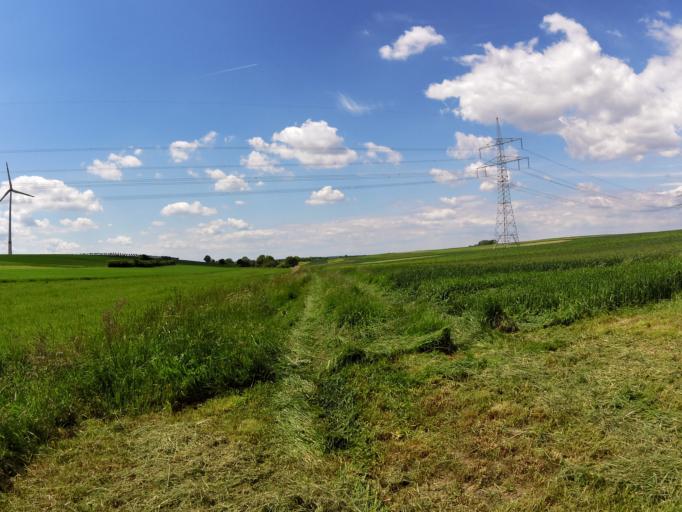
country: DE
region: Bavaria
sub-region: Regierungsbezirk Unterfranken
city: Theilheim
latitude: 49.7248
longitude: 10.0535
